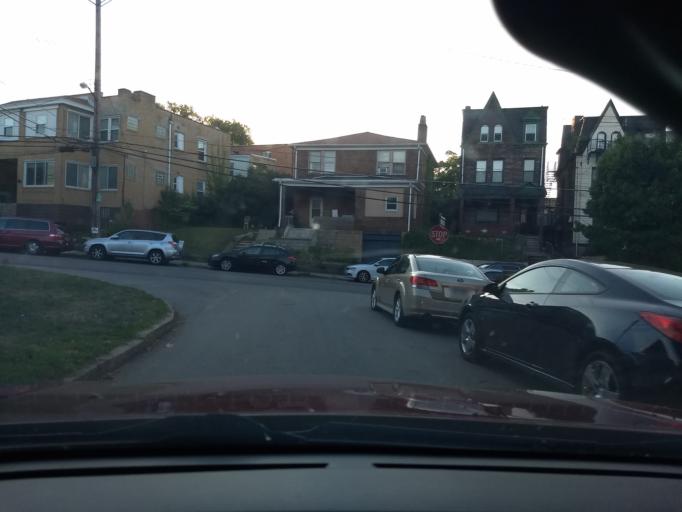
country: US
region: Pennsylvania
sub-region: Allegheny County
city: Bloomfield
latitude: 40.4373
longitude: -79.9520
